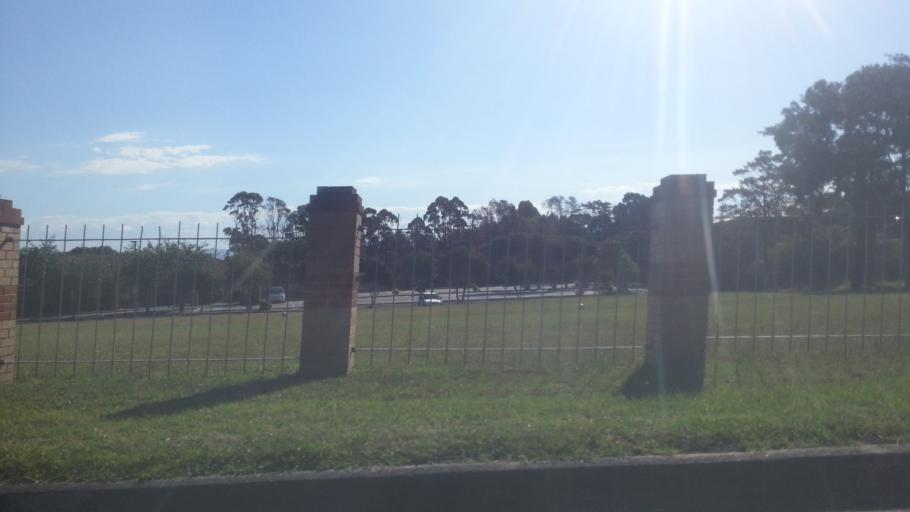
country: AU
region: New South Wales
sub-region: Wollongong
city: Berkeley
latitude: -34.4753
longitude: 150.8547
